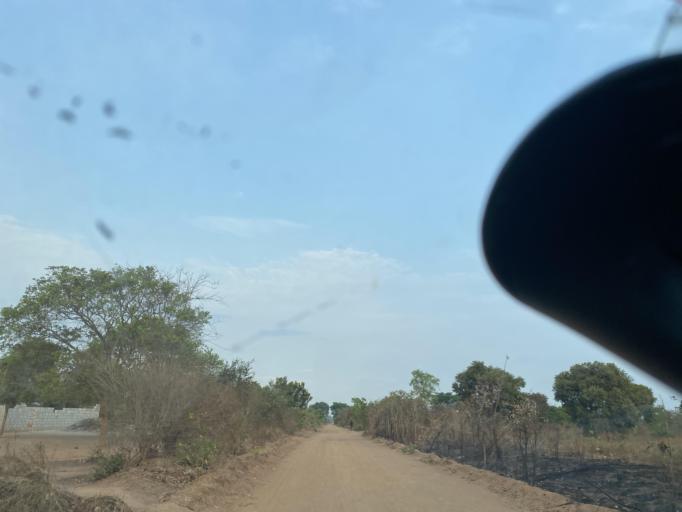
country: ZM
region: Lusaka
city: Chongwe
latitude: -15.2024
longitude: 28.5233
